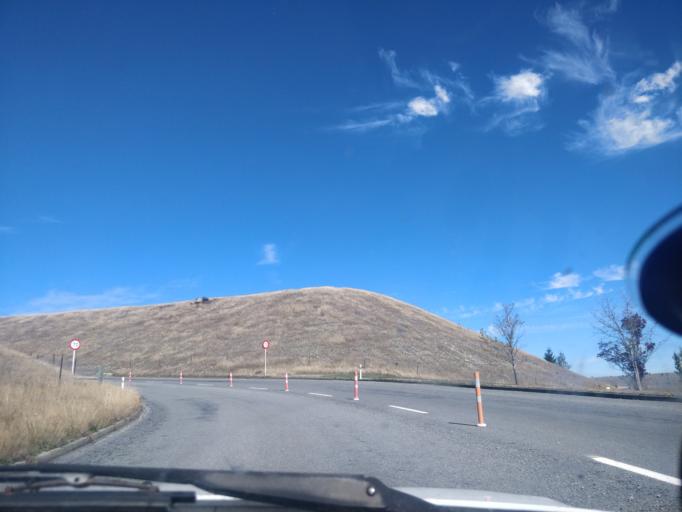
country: NZ
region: Otago
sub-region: Queenstown-Lakes District
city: Wanaka
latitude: -44.2654
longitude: 170.0330
